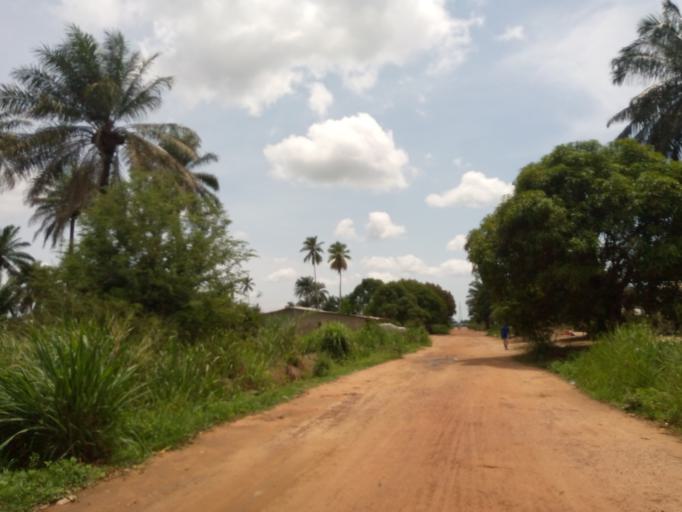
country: SL
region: Western Area
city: Waterloo
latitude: 8.3551
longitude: -12.9629
